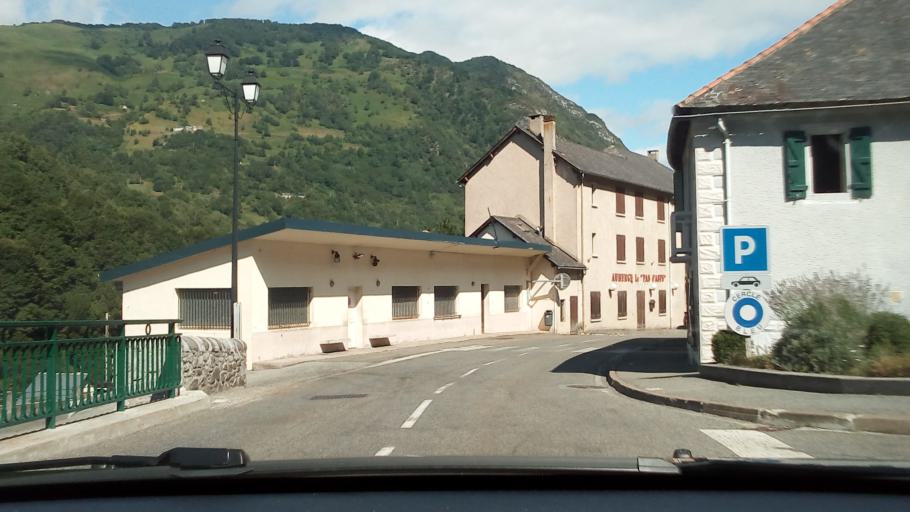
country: ES
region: Aragon
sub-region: Provincia de Huesca
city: Canfranc
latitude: 42.8710
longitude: -0.5541
